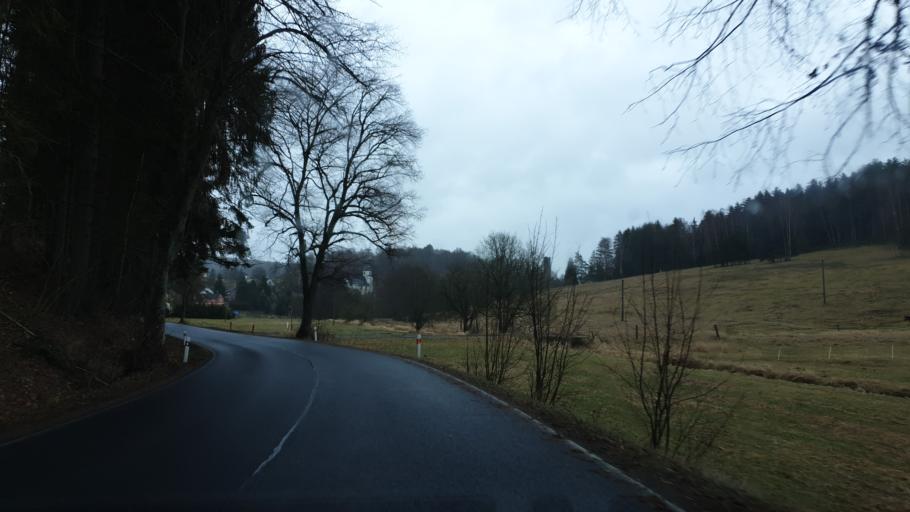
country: CZ
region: Karlovarsky
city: As
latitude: 50.2523
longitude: 12.1992
